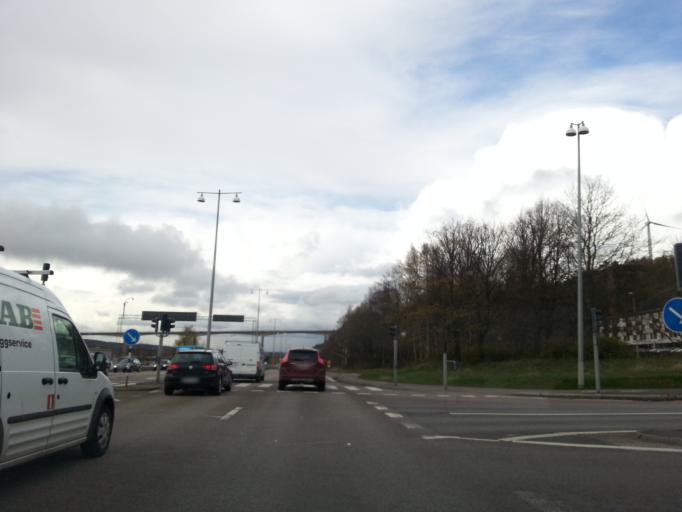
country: SE
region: Vaestra Goetaland
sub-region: Goteborg
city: Gardsten
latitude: 57.7894
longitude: 12.0157
